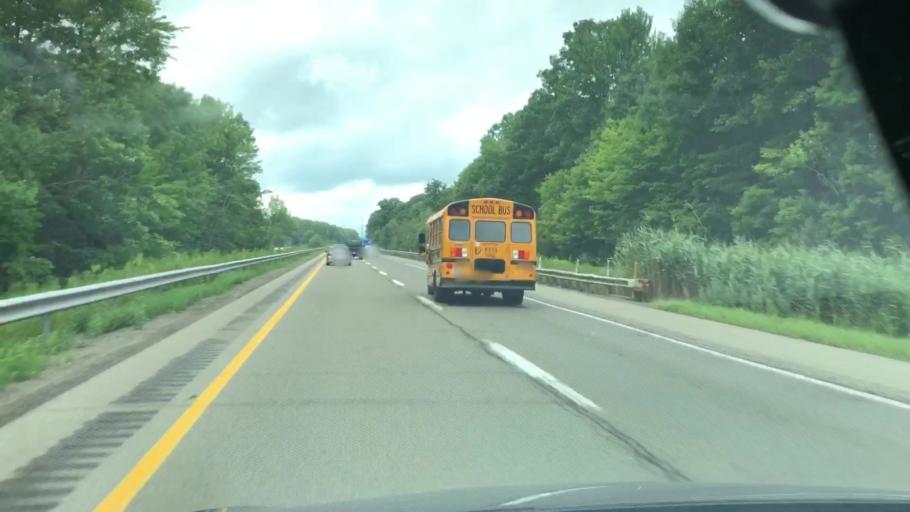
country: US
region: Pennsylvania
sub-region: Erie County
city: Edinboro
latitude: 41.8527
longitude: -80.1754
